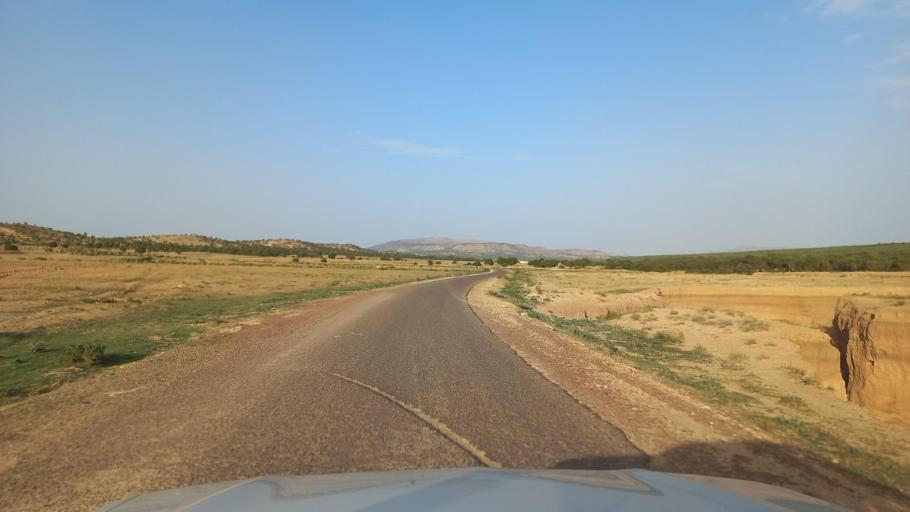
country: TN
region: Al Qasrayn
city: Kasserine
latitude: 35.3916
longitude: 8.8706
